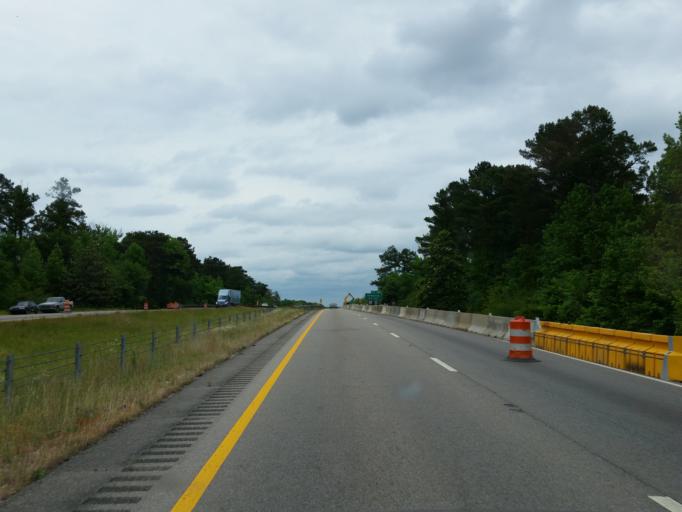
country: US
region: Alabama
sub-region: Sumter County
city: York
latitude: 32.4204
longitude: -88.4558
